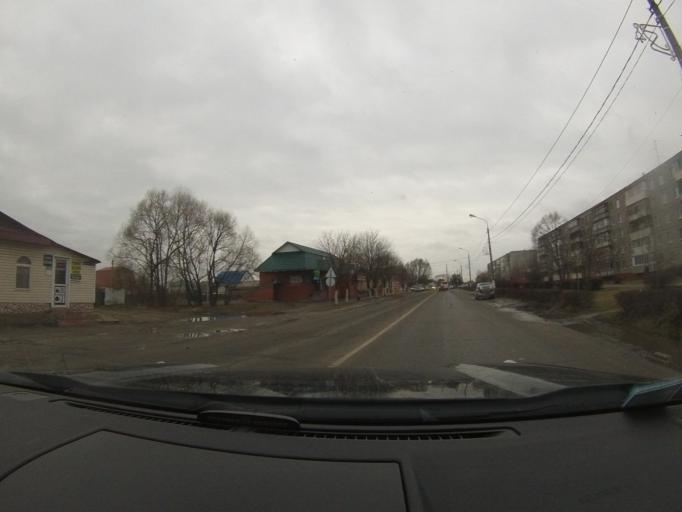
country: RU
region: Moskovskaya
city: Lopatinskiy
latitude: 55.3365
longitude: 38.7135
